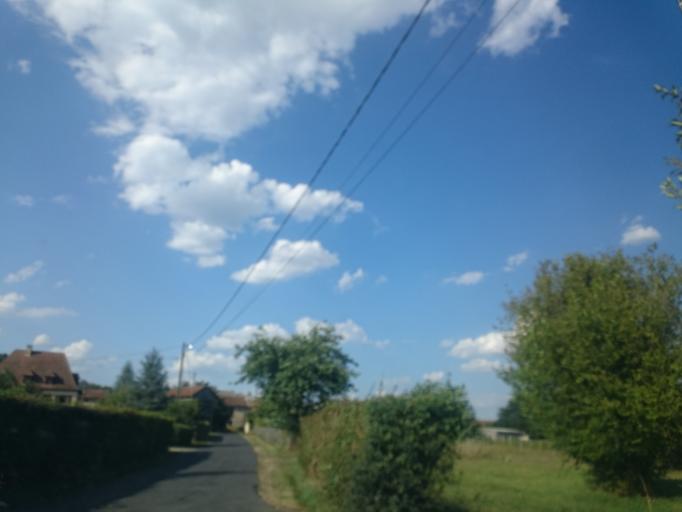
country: FR
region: Auvergne
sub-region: Departement du Cantal
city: Laroquebrou
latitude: 44.8998
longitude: 2.1796
